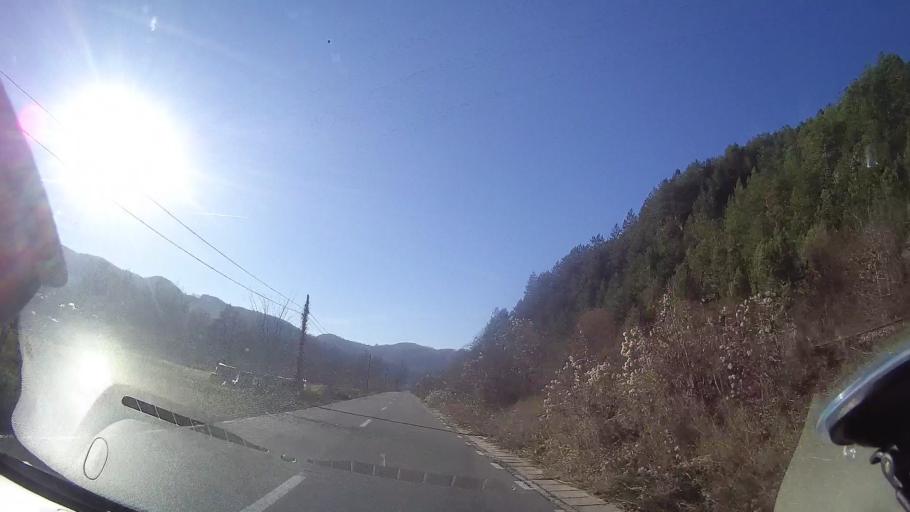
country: RO
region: Bihor
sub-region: Comuna Bratca
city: Bratca
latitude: 46.9270
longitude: 22.6308
